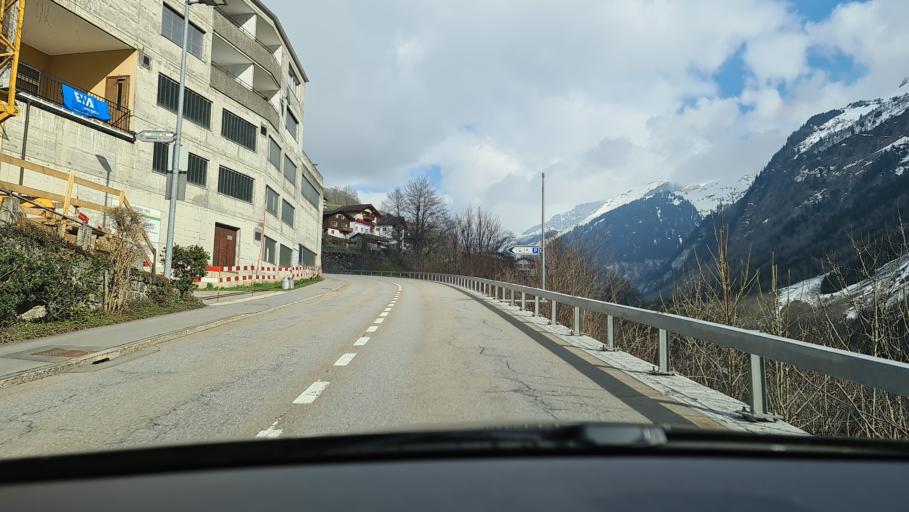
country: CH
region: Uri
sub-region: Uri
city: Burglen
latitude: 46.8723
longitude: 8.7306
